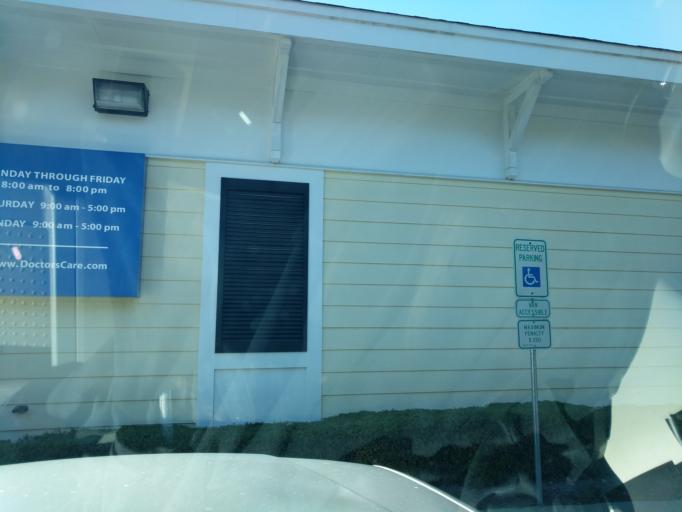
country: US
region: South Carolina
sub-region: Greenville County
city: Greer
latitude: 34.9492
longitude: -82.2328
